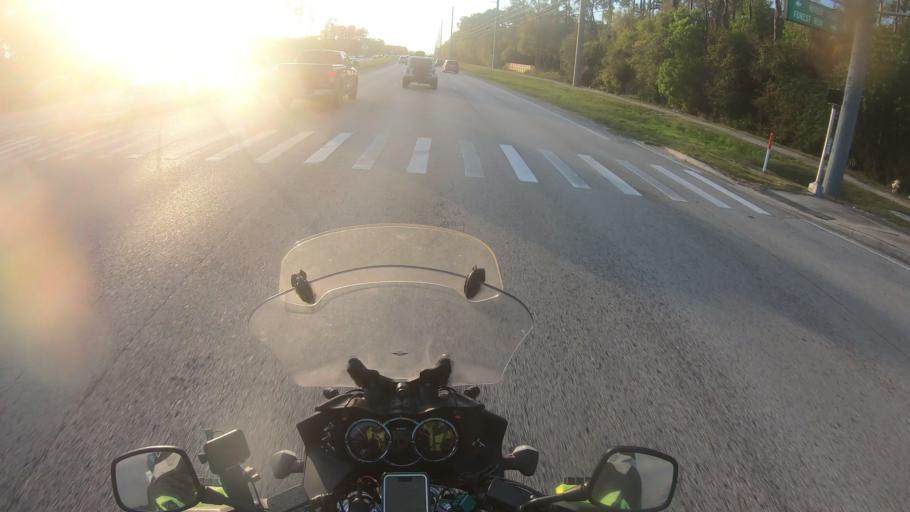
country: US
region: Florida
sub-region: Sarasota County
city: The Meadows
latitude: 27.4339
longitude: -82.4342
